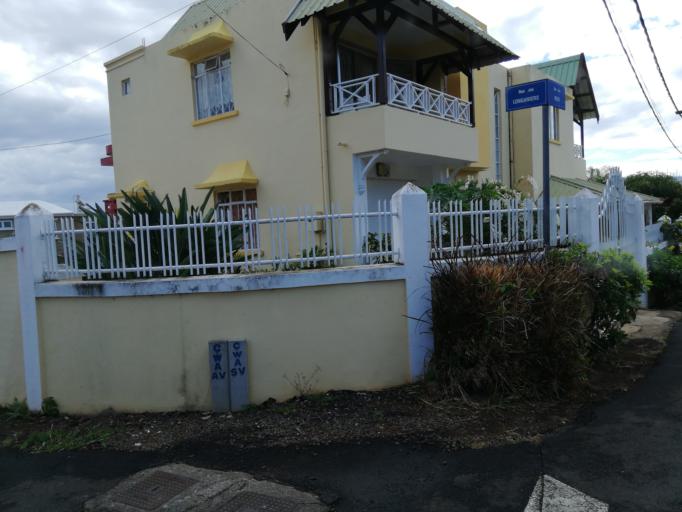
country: MU
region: Black River
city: Petite Riviere
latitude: -20.2026
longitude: 57.4670
